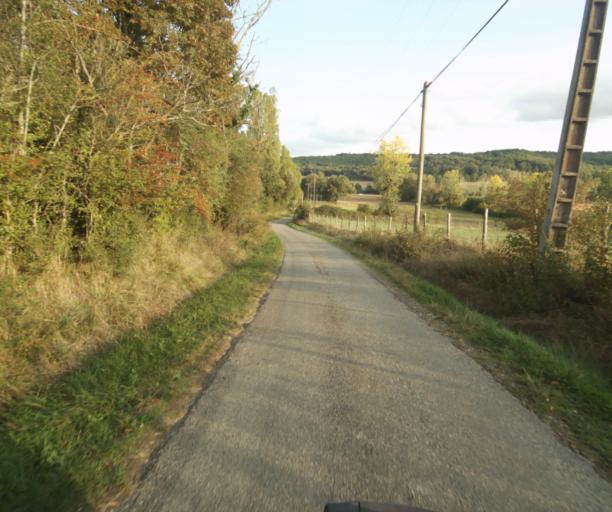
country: FR
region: Midi-Pyrenees
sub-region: Departement de la Haute-Garonne
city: Launac
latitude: 43.8195
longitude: 1.1214
